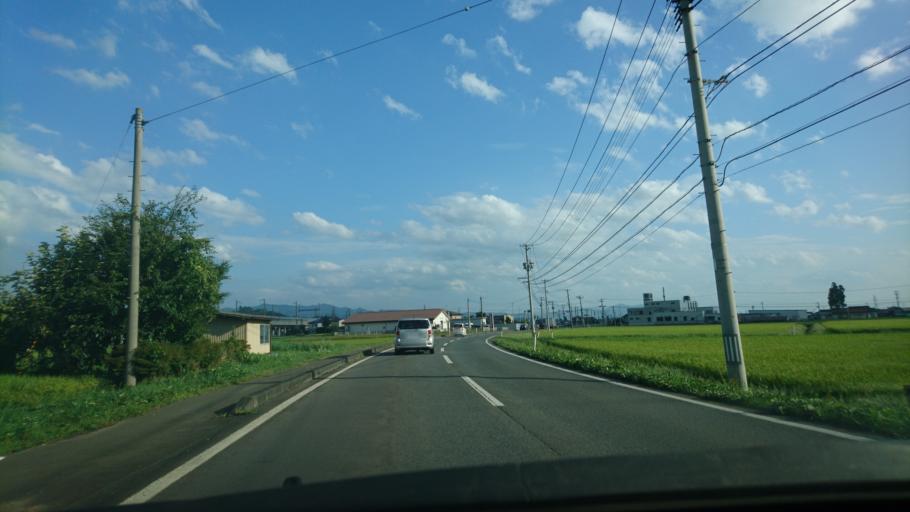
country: JP
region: Iwate
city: Mizusawa
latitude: 39.1663
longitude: 141.1801
